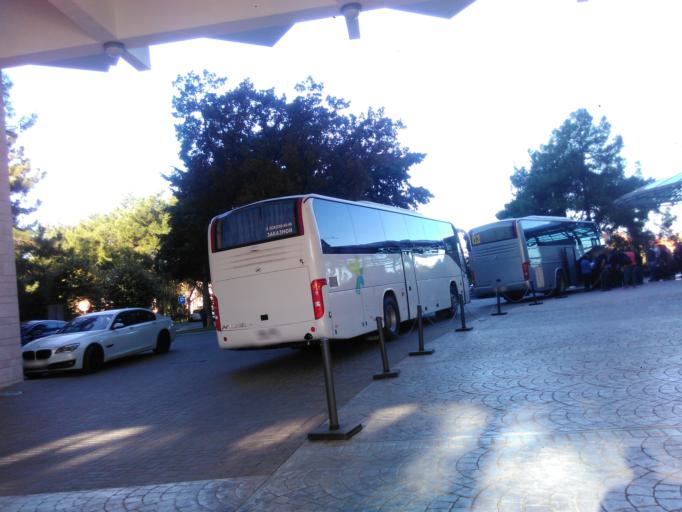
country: RU
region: Krasnodarskiy
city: Gelendzhik
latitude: 44.5509
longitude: 38.0542
